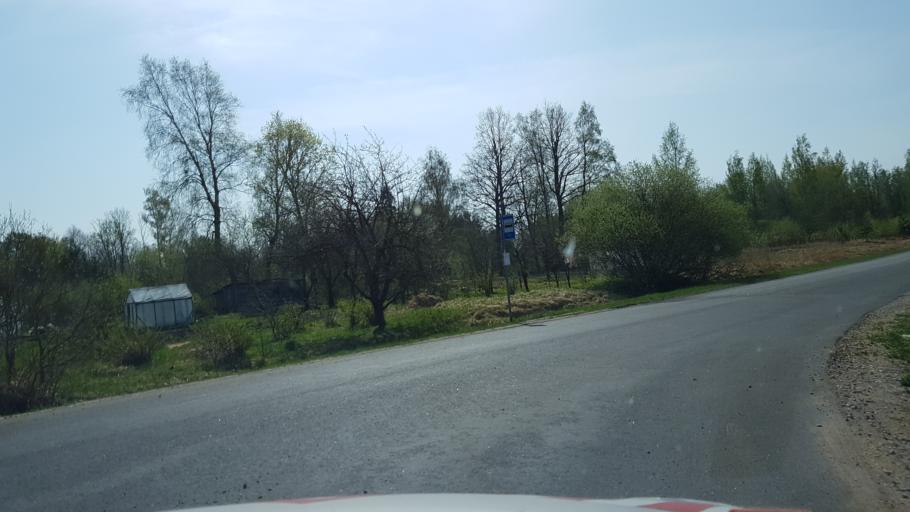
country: EE
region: Paernumaa
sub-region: Sindi linn
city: Sindi
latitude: 58.4266
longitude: 24.6518
